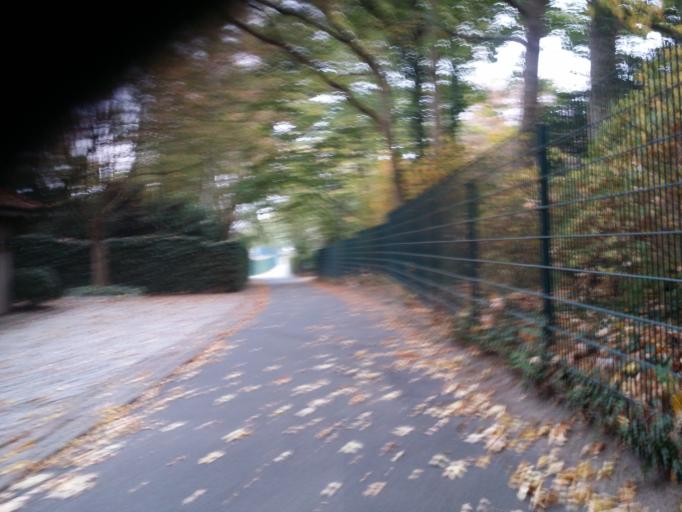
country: DE
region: Lower Saxony
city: Lemwerder
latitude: 53.1649
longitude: 8.6312
